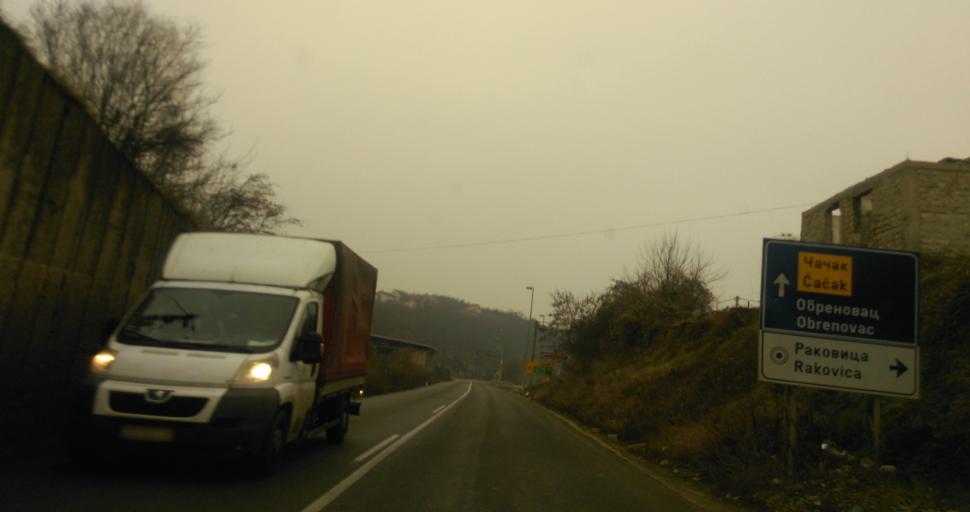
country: RS
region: Central Serbia
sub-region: Belgrade
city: Rakovica
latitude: 44.7230
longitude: 20.4539
